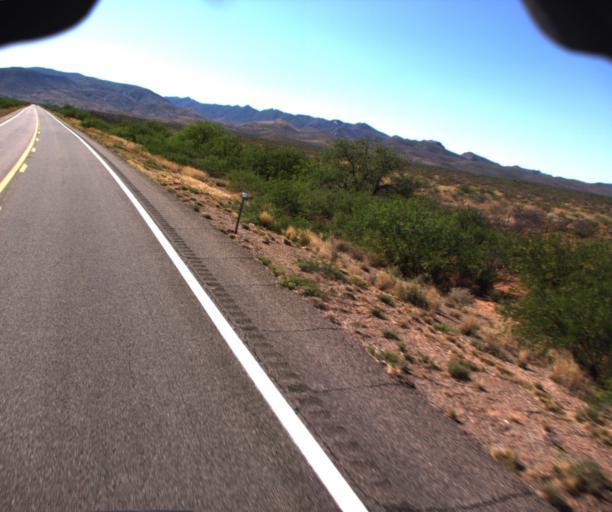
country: US
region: Arizona
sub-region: Cochise County
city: Bisbee
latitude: 31.5652
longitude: -110.0254
